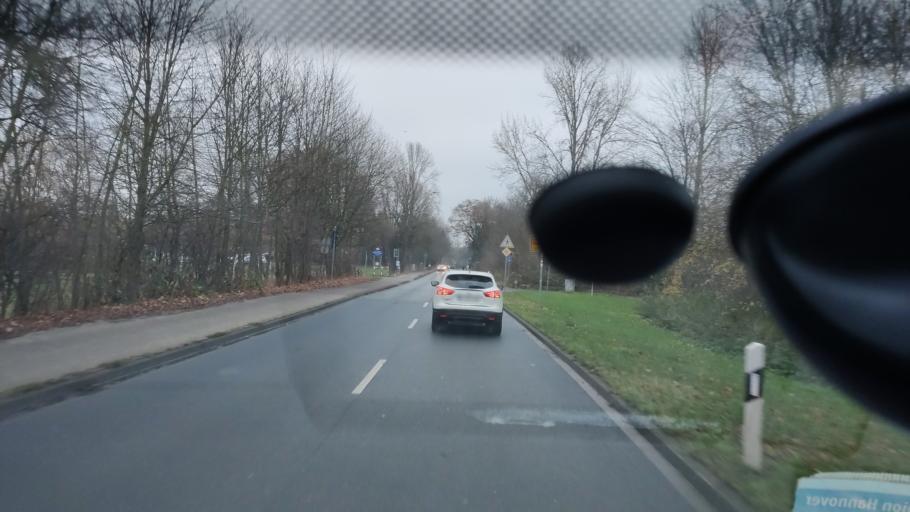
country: DE
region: Lower Saxony
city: Hemmingen
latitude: 52.3314
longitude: 9.7549
